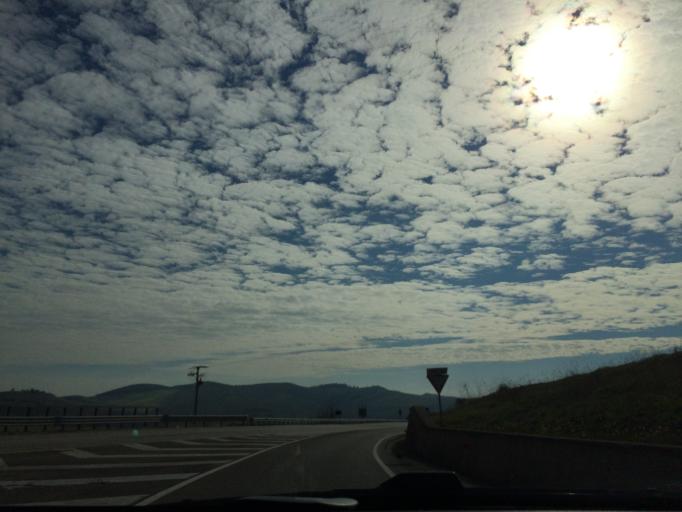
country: IT
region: Basilicate
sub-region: Provincia di Matera
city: Matera
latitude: 40.6430
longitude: 16.5941
